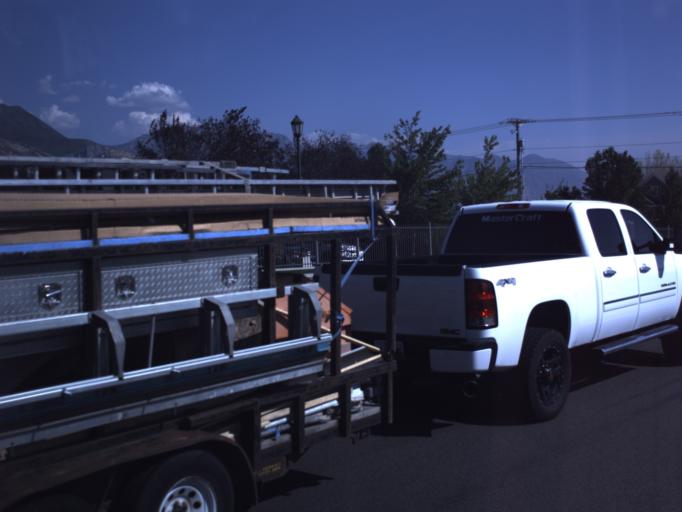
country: US
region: Utah
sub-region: Utah County
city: Cedar Hills
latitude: 40.3926
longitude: -111.7693
